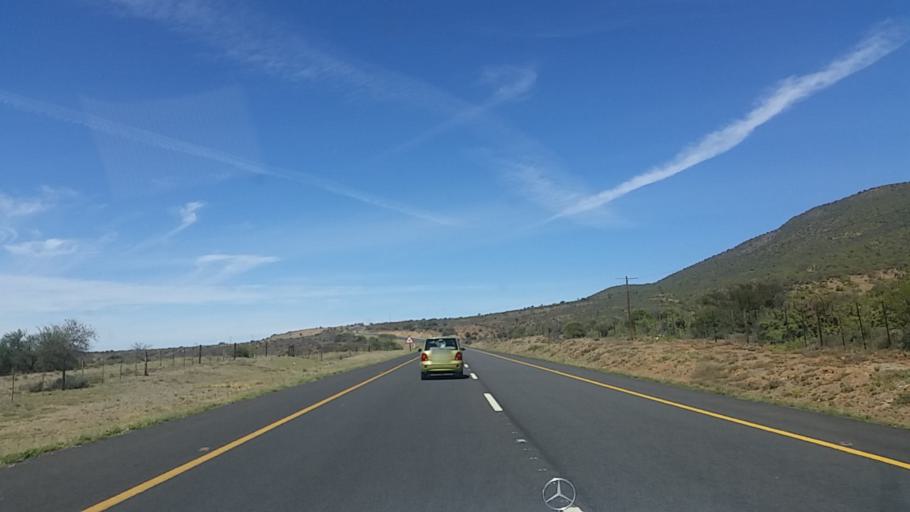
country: ZA
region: Eastern Cape
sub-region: Cacadu District Municipality
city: Graaff-Reinet
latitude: -32.2846
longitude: 24.5384
